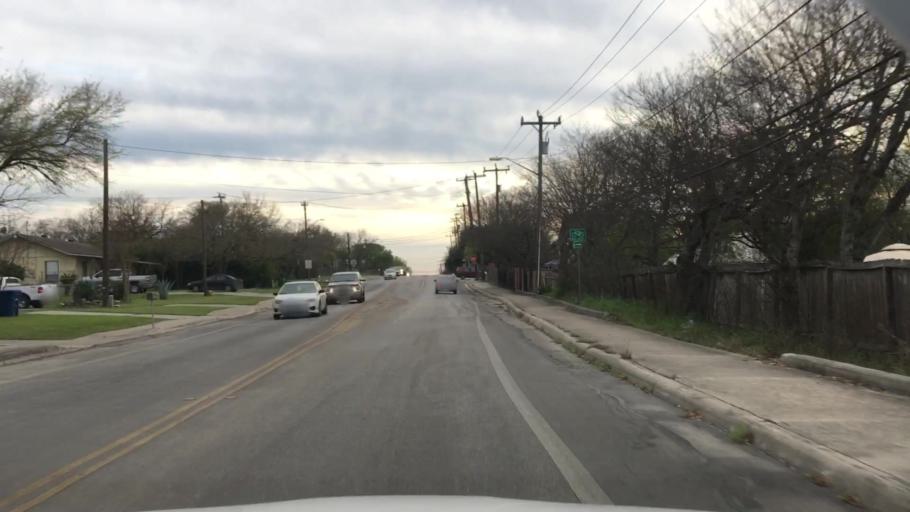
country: US
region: Texas
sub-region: Bexar County
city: Windcrest
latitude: 29.5604
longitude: -98.4016
